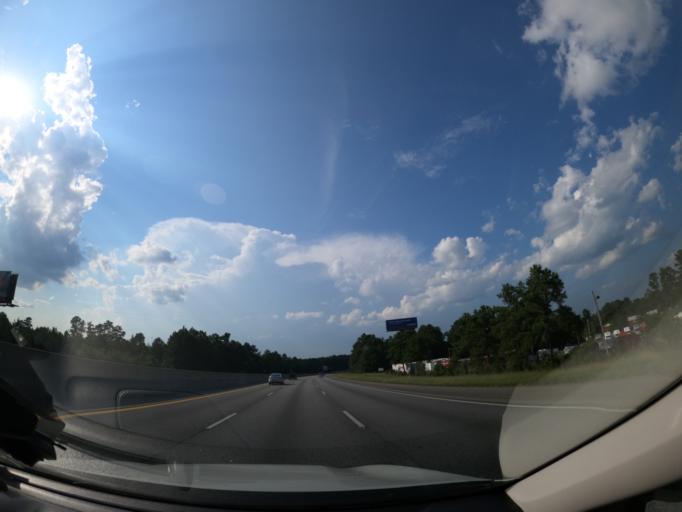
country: US
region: Georgia
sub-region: Columbia County
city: Martinez
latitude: 33.4347
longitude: -82.0702
